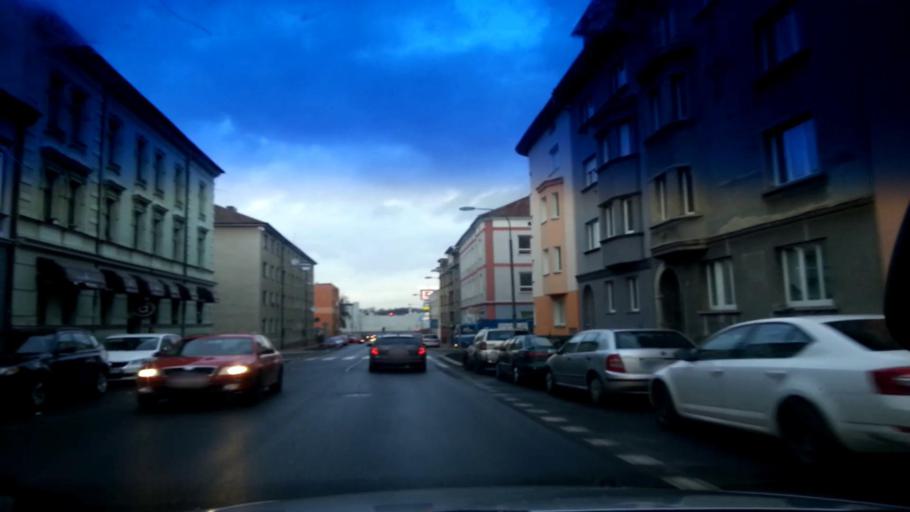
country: CZ
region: Karlovarsky
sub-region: Okres Cheb
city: Cheb
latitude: 50.0758
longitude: 12.3786
